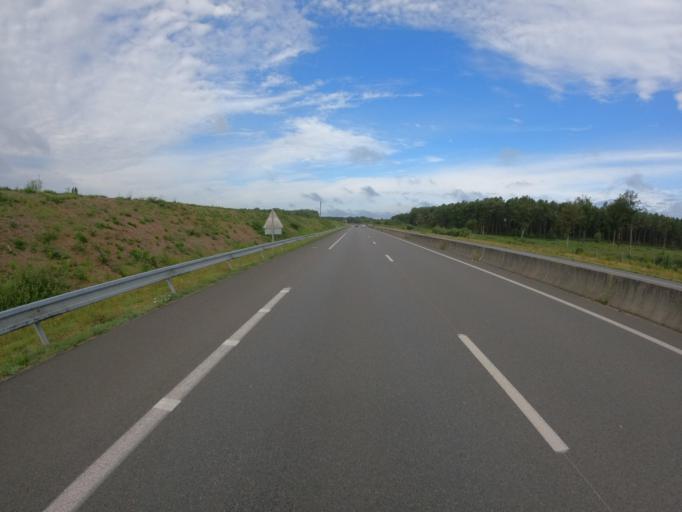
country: FR
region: Centre
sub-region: Departement d'Indre-et-Loire
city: Langeais
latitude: 47.3466
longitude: 0.3773
